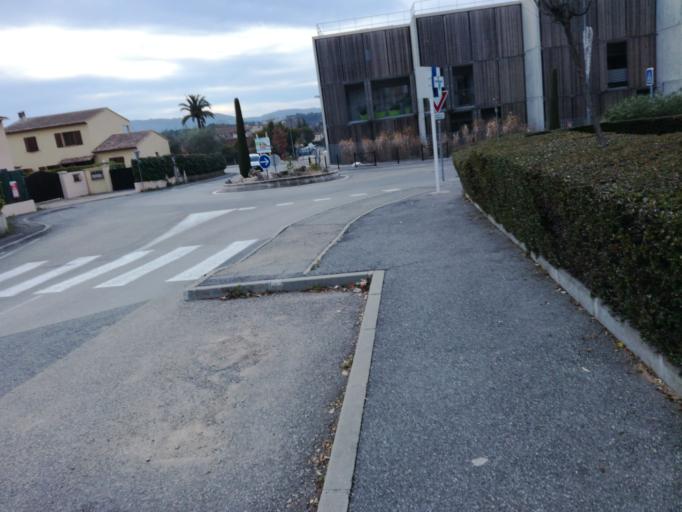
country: FR
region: Provence-Alpes-Cote d'Azur
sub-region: Departement des Alpes-Maritimes
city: Mouans-Sartoux
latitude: 43.6180
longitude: 6.9763
